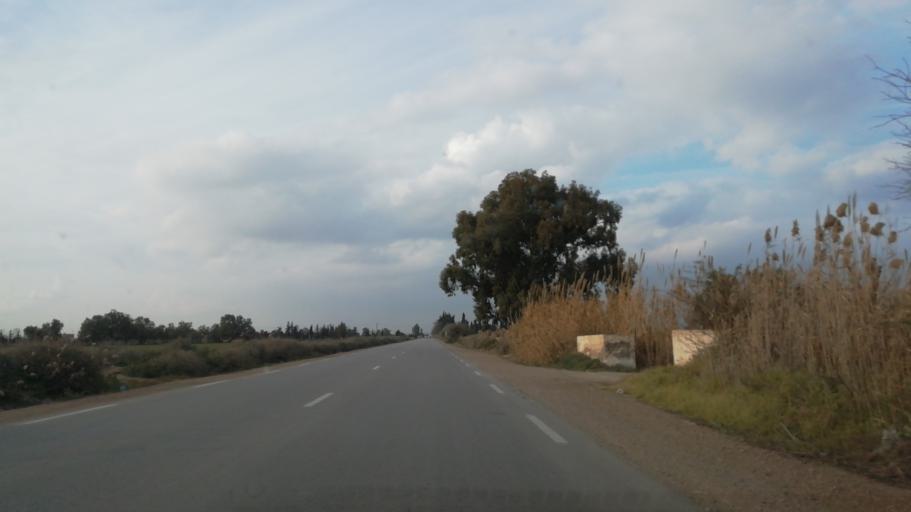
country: DZ
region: Mascara
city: Sig
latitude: 35.6750
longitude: -0.0061
